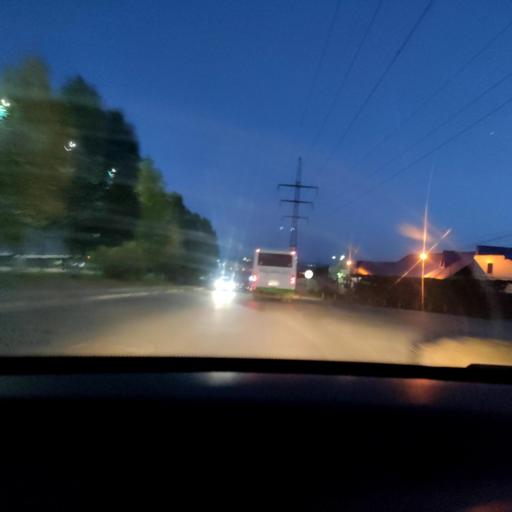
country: RU
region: Samara
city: Samara
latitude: 53.1838
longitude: 50.1732
